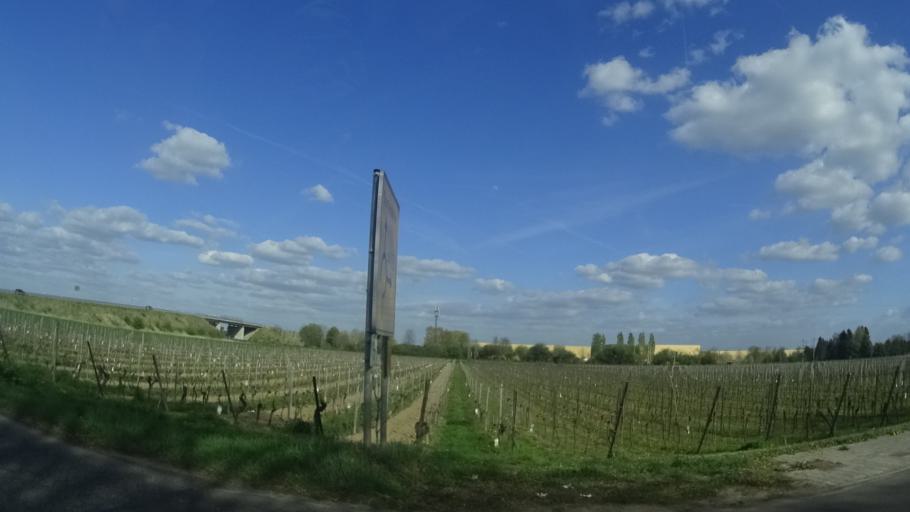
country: DE
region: Rheinland-Pfalz
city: Alsheim
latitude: 49.7715
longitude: 8.3417
